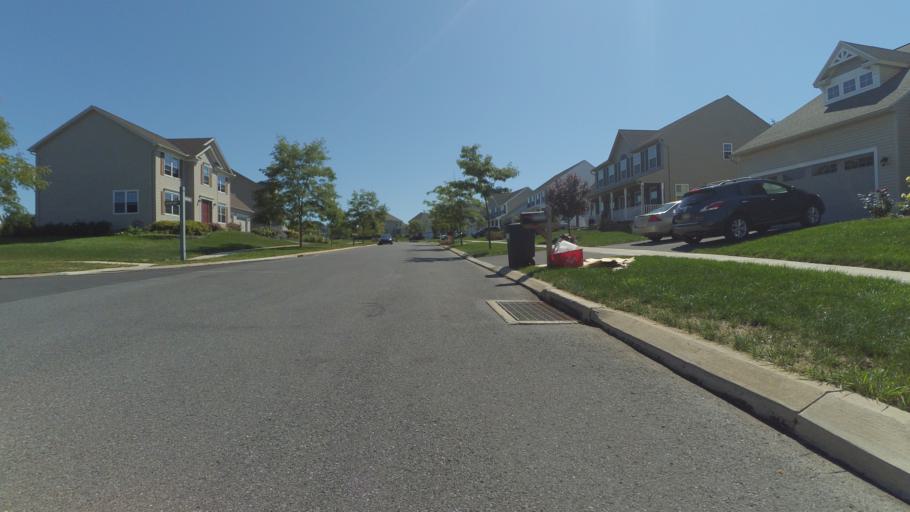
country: US
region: Pennsylvania
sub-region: Centre County
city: Pine Grove Mills
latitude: 40.7661
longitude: -77.8953
